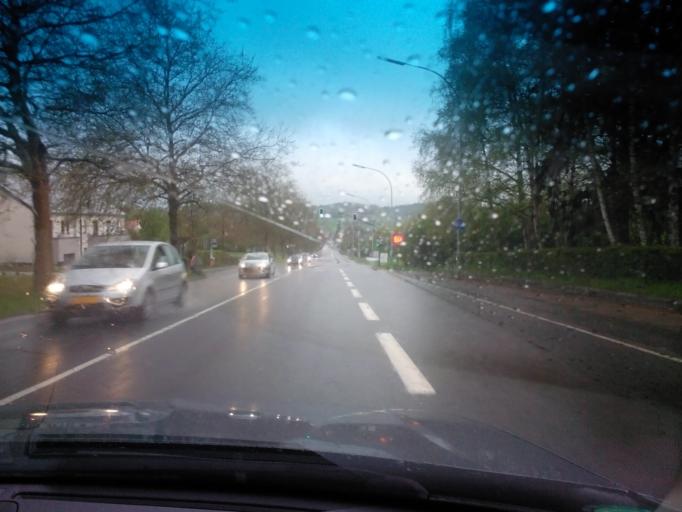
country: LU
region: Grevenmacher
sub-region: Canton de Grevenmacher
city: Junglinster
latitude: 49.7158
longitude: 6.2624
